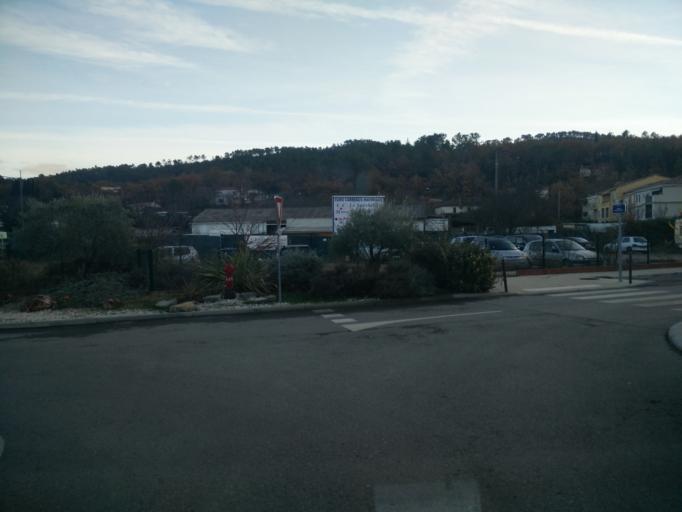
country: FR
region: Provence-Alpes-Cote d'Azur
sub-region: Departement du Var
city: Brignoles
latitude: 43.4025
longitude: 6.0657
